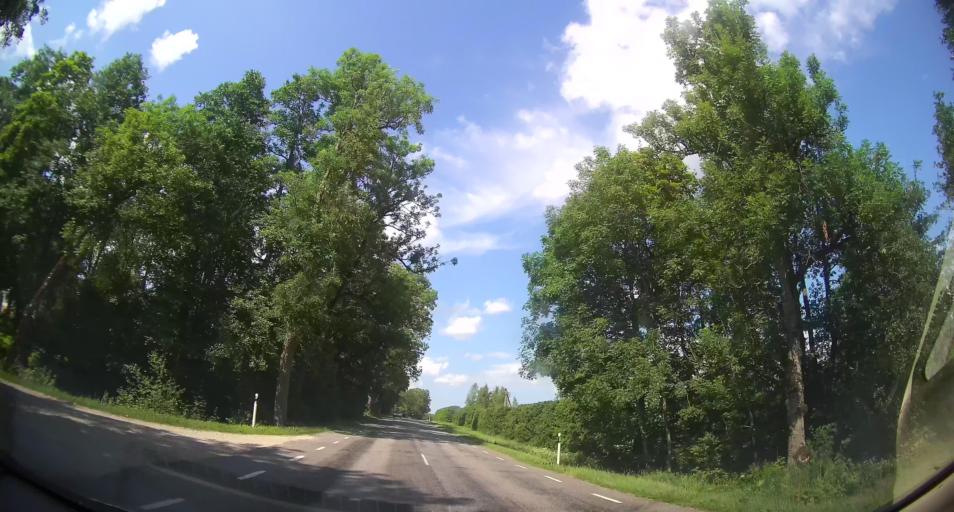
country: EE
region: Harju
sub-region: Nissi vald
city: Turba
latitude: 58.8943
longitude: 24.2407
